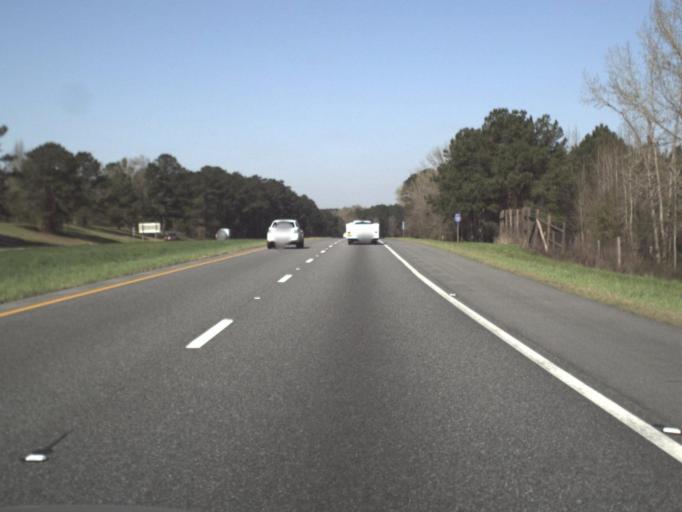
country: US
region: Florida
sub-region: Gadsden County
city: Quincy
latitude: 30.5408
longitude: -84.6025
